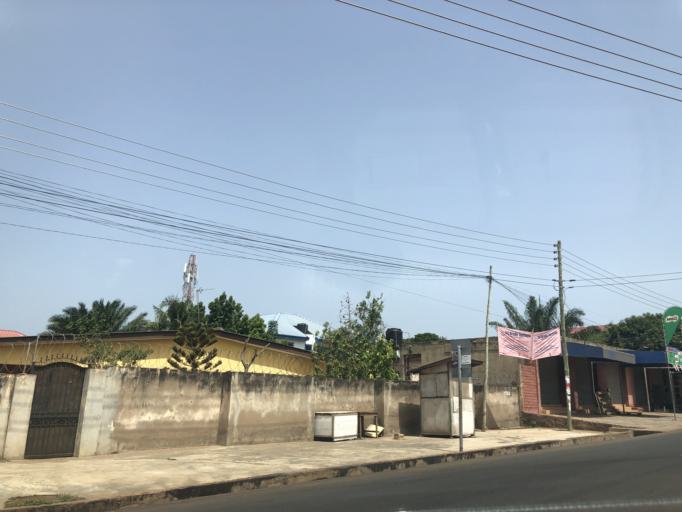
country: GH
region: Greater Accra
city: Dome
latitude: 5.6194
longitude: -0.2501
